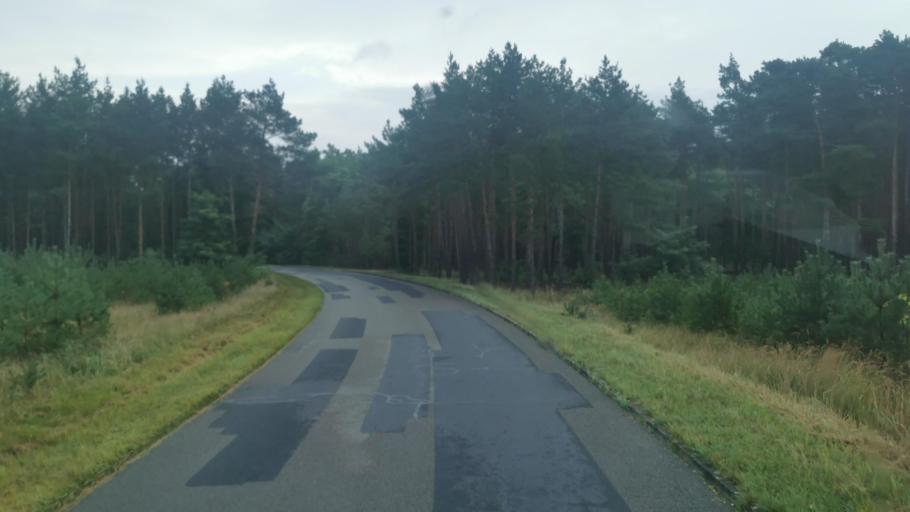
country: DE
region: Brandenburg
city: Kolkwitz
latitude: 51.7274
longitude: 14.2268
